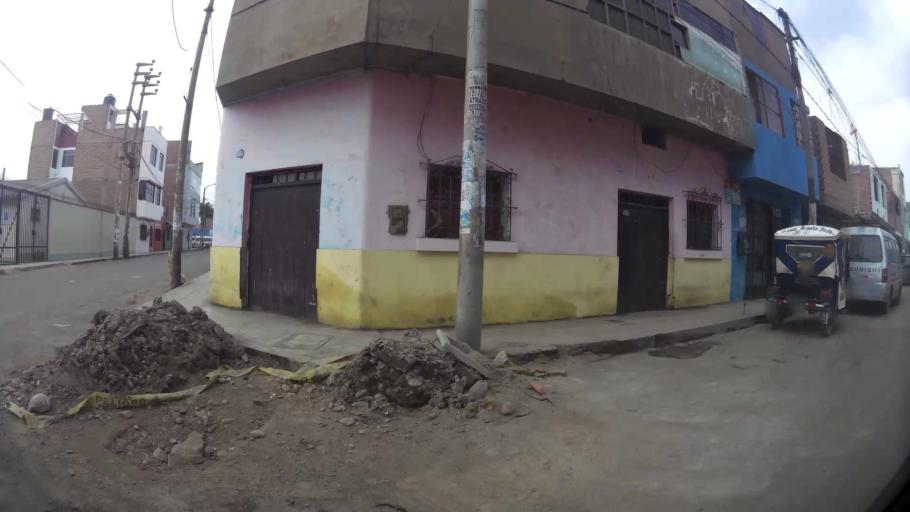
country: PE
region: Lima
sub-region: Provincia de Huaral
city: Huaral
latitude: -11.4914
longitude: -77.2103
